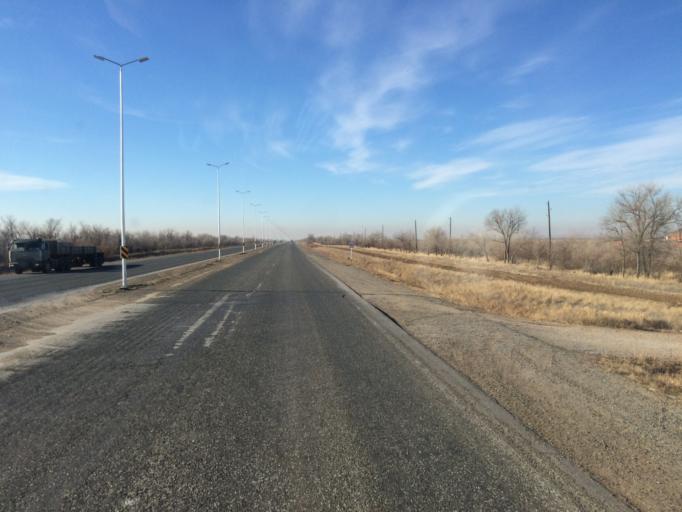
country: KZ
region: Aqtoebe
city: Aqtobe
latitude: 50.2913
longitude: 57.3541
